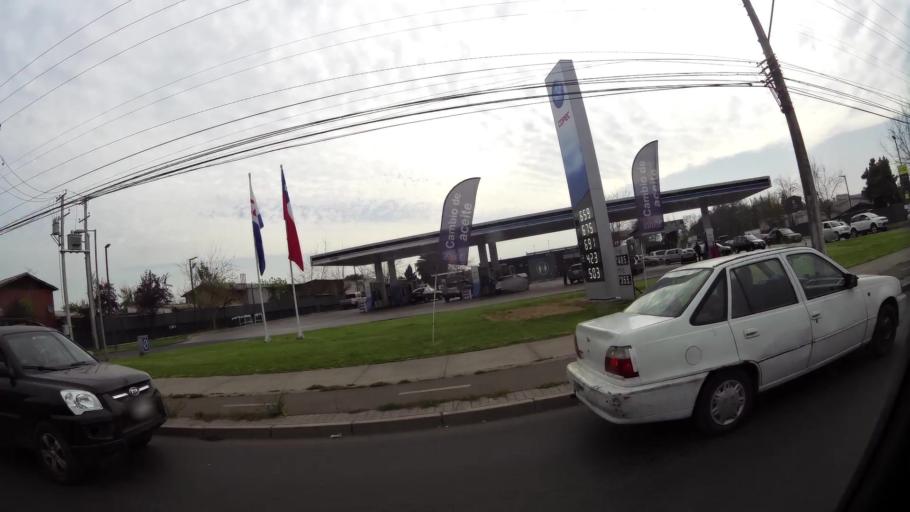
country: CL
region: Santiago Metropolitan
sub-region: Provincia de Santiago
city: Lo Prado
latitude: -33.5214
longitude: -70.7556
